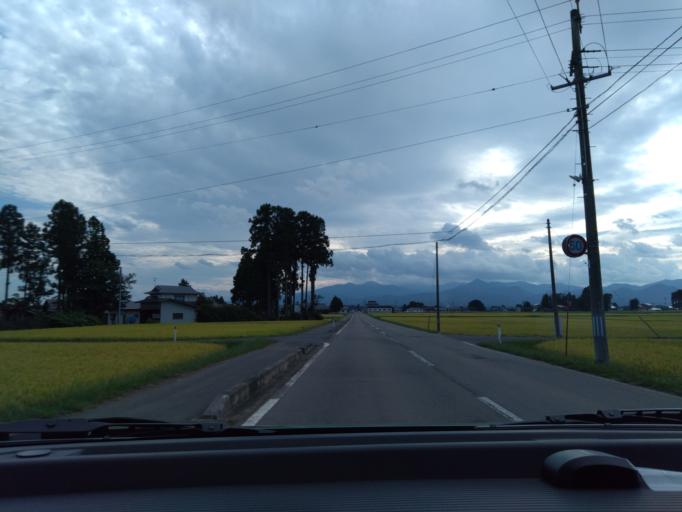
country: JP
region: Iwate
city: Kitakami
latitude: 39.3194
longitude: 141.0604
